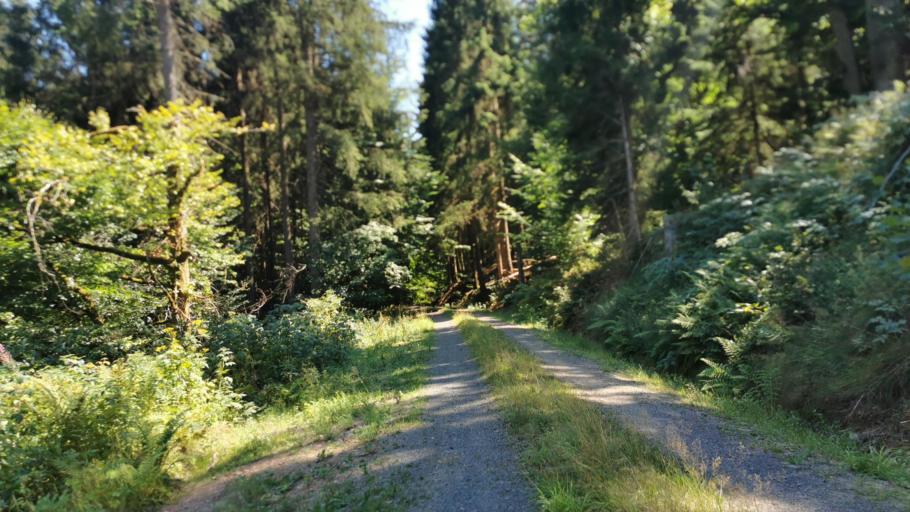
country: DE
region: Bavaria
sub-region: Upper Franconia
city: Pressig
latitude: 50.3950
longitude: 11.2945
